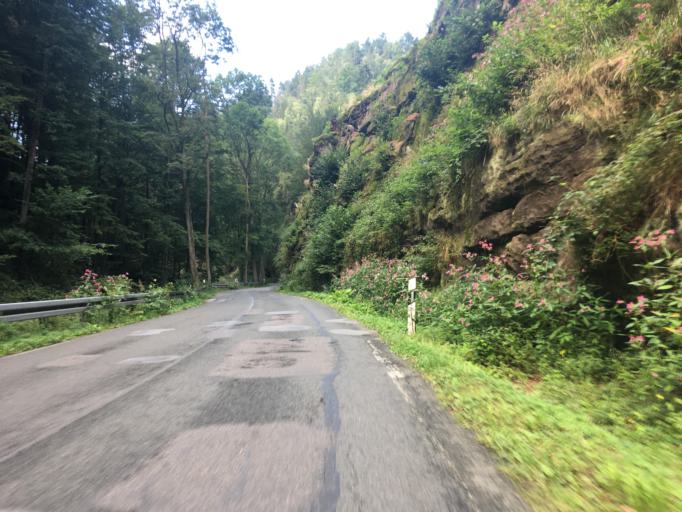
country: DE
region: Saxony
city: Sebnitz
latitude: 50.9299
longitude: 14.2681
